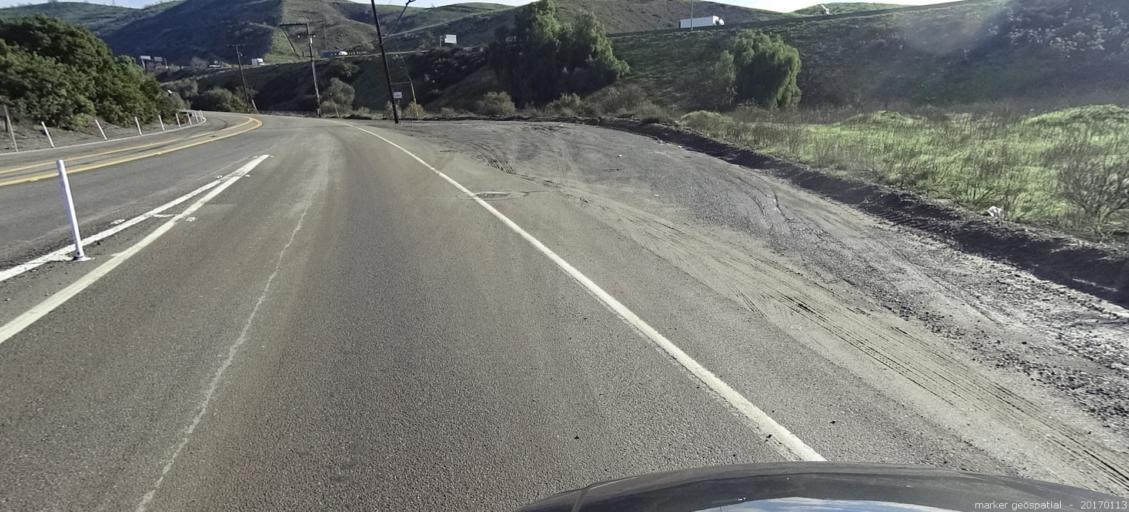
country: US
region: California
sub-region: Orange County
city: Brea
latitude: 33.9407
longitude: -117.8777
